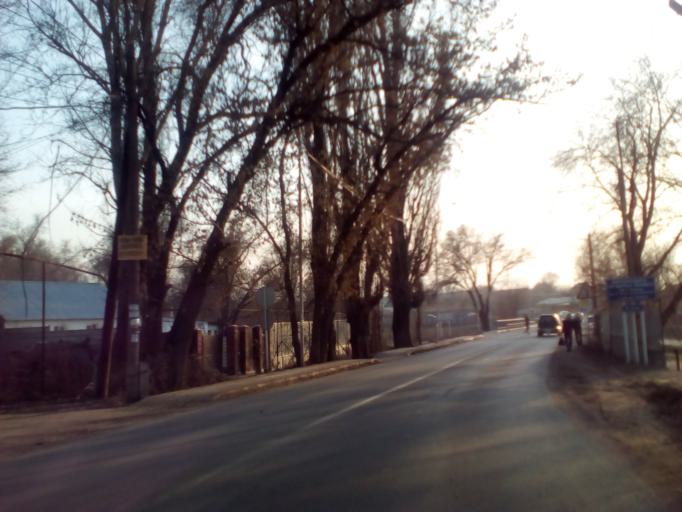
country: KZ
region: Almaty Oblysy
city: Burunday
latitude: 43.2519
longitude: 76.7656
